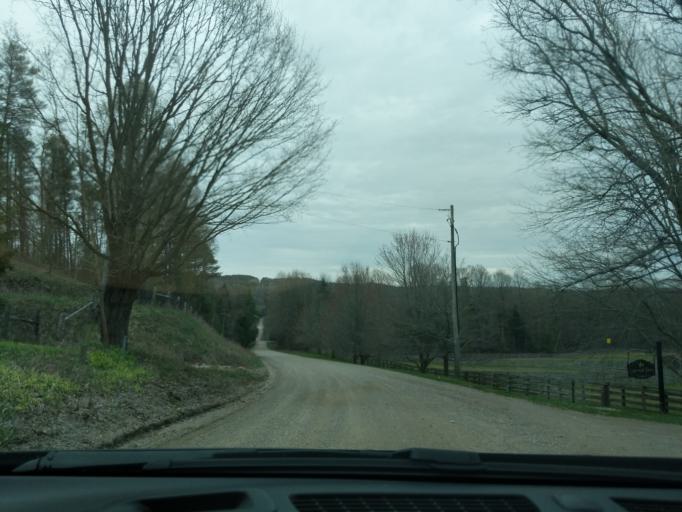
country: CA
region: Ontario
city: Orangeville
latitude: 44.0013
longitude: -80.0161
